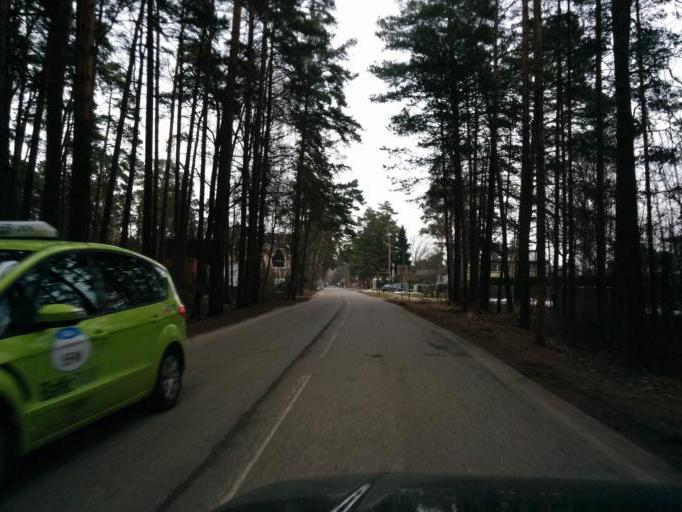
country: LV
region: Babite
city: Pinki
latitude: 56.9914
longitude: 23.9121
